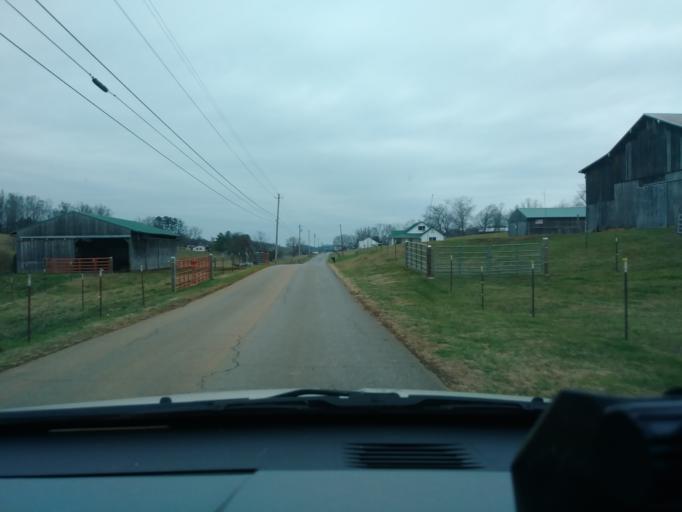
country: US
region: Tennessee
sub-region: Greene County
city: Greeneville
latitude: 36.1041
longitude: -82.8908
